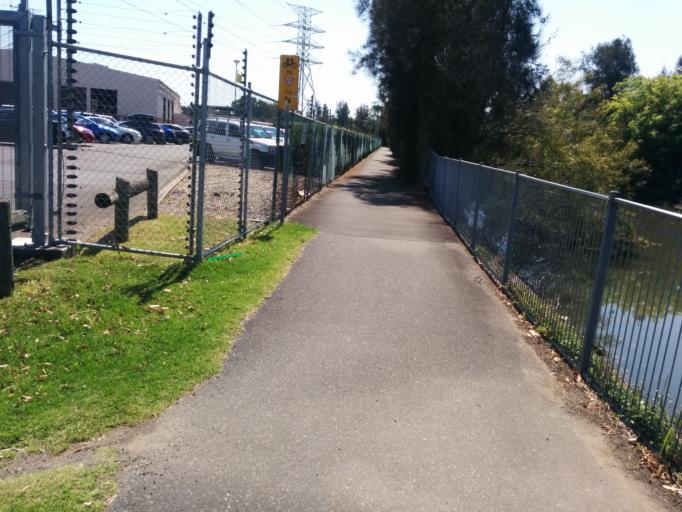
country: AU
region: New South Wales
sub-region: Strathfield
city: Homebush
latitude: -33.8581
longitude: 151.0841
